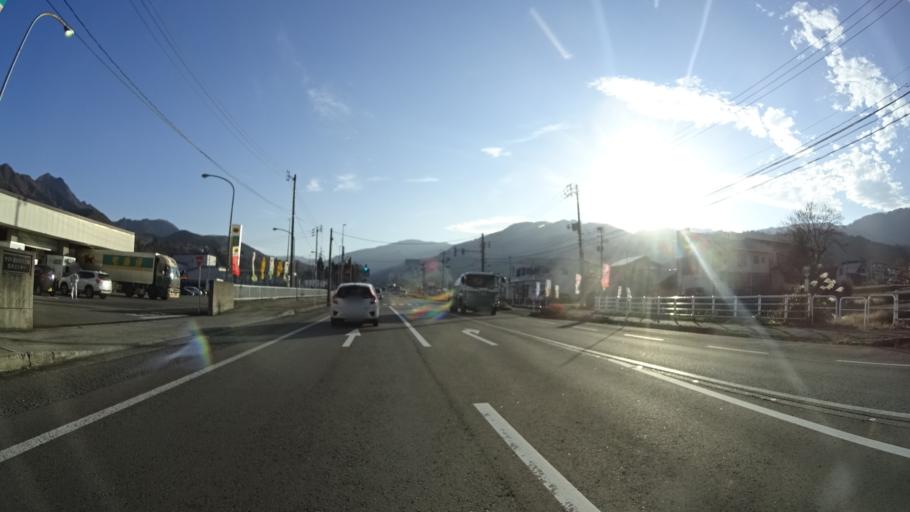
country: JP
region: Niigata
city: Shiozawa
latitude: 36.9866
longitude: 138.8085
